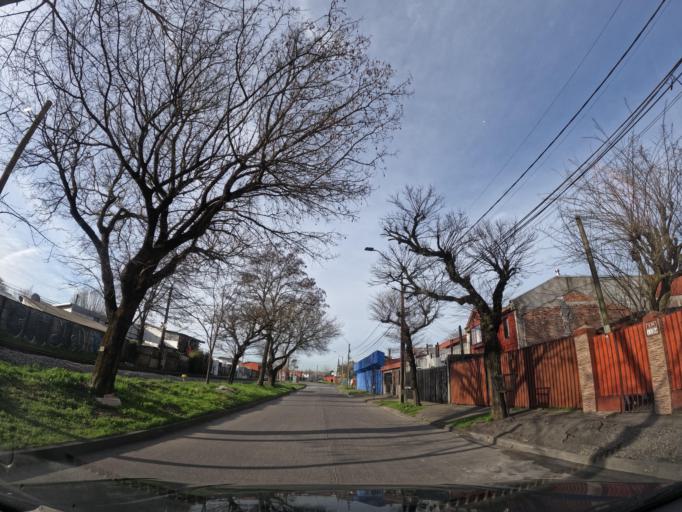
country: CL
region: Biobio
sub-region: Provincia de Concepcion
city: Concepcion
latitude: -36.8129
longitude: -73.0513
